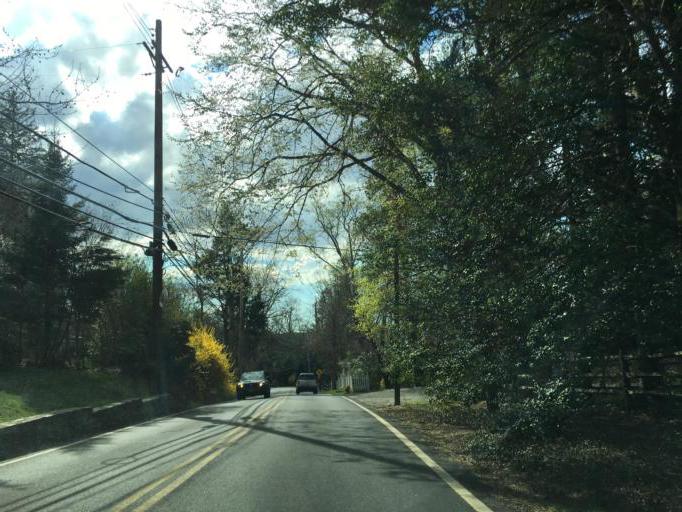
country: US
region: Maryland
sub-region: Baltimore County
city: Mays Chapel
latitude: 39.4013
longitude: -76.6573
